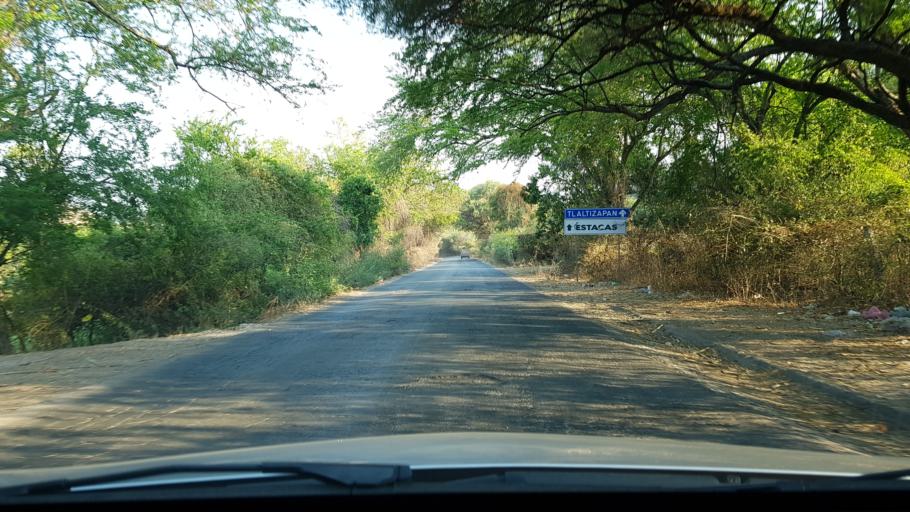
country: MX
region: Morelos
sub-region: Tepalcingo
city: Zacapalco
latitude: 18.6390
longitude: -99.0176
